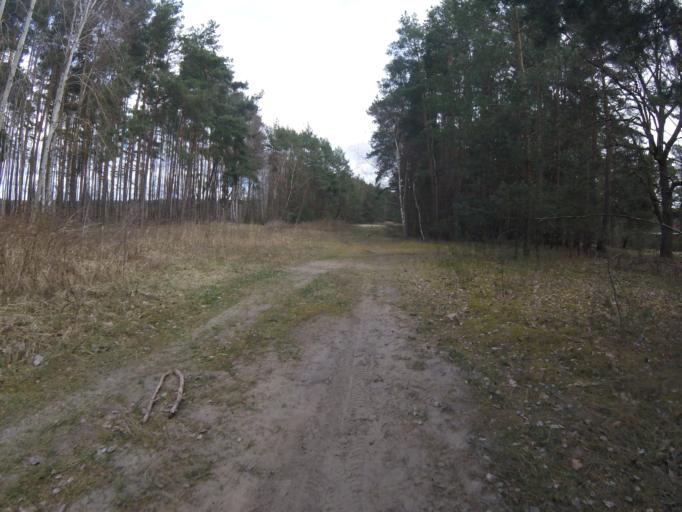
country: DE
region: Brandenburg
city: Gross Koris
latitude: 52.1804
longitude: 13.6412
